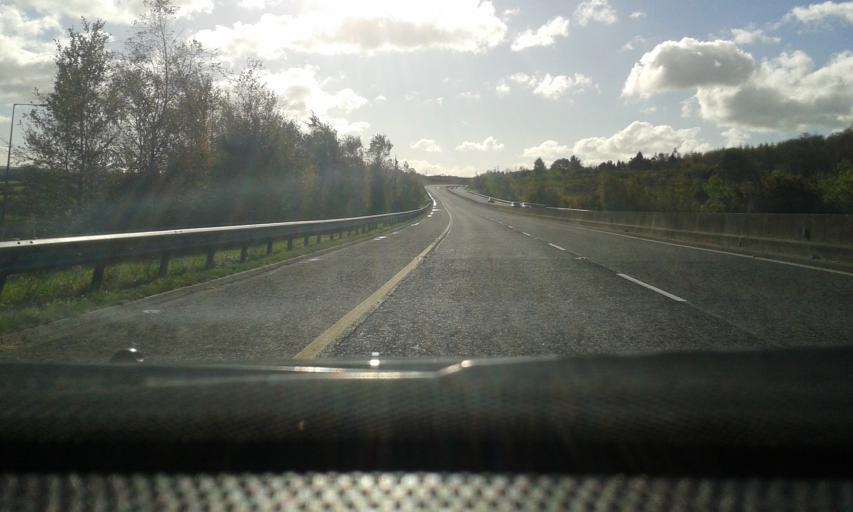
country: IE
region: Munster
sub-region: County Cork
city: Fermoy
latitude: 52.1165
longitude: -8.2723
